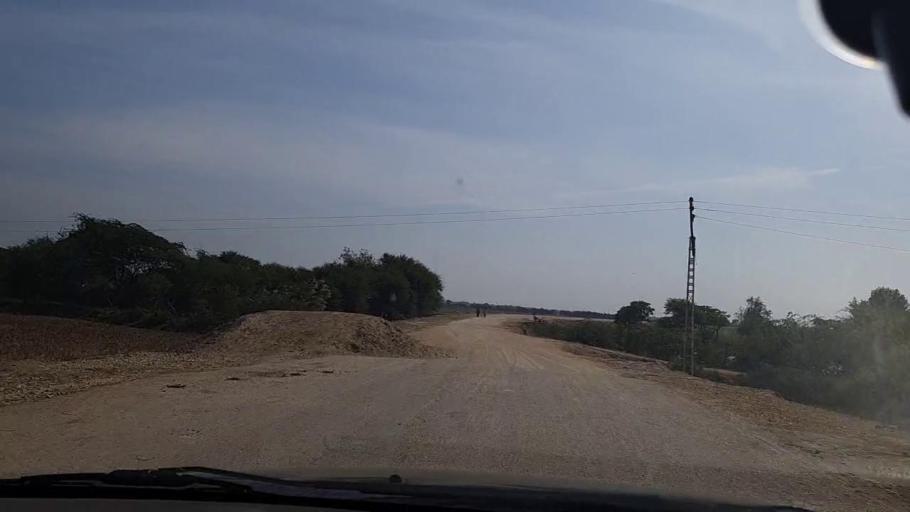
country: PK
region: Sindh
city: Mirpur Batoro
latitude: 24.7325
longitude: 68.2753
